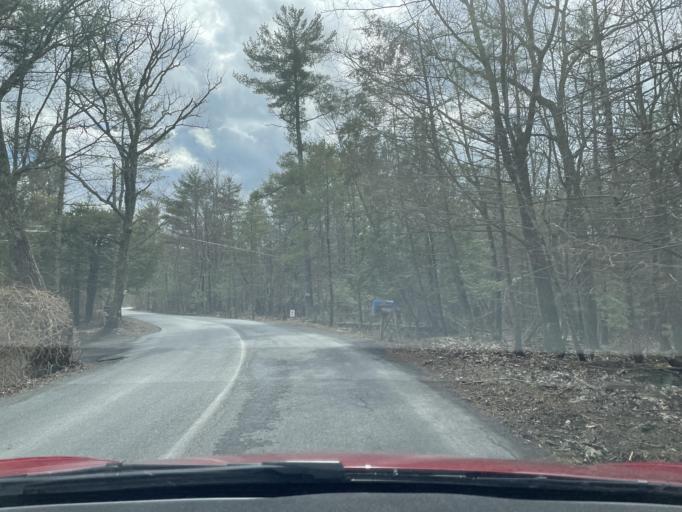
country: US
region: New York
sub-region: Ulster County
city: Zena
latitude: 42.0361
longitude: -74.0375
